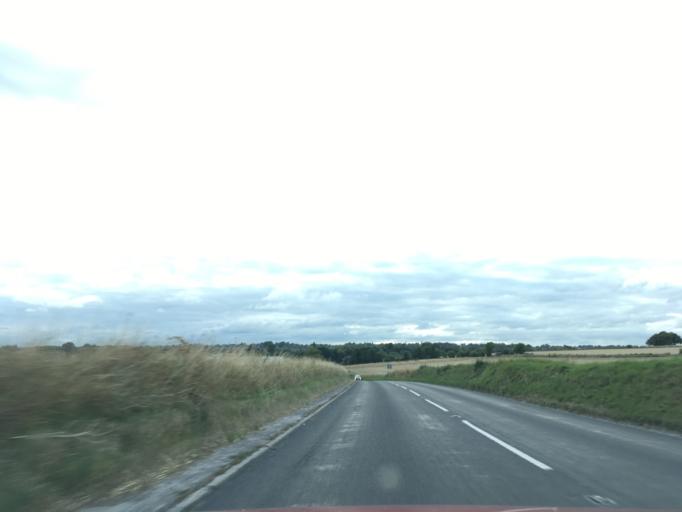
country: GB
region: England
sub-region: Wiltshire
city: Devizes
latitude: 51.3377
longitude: -1.9599
